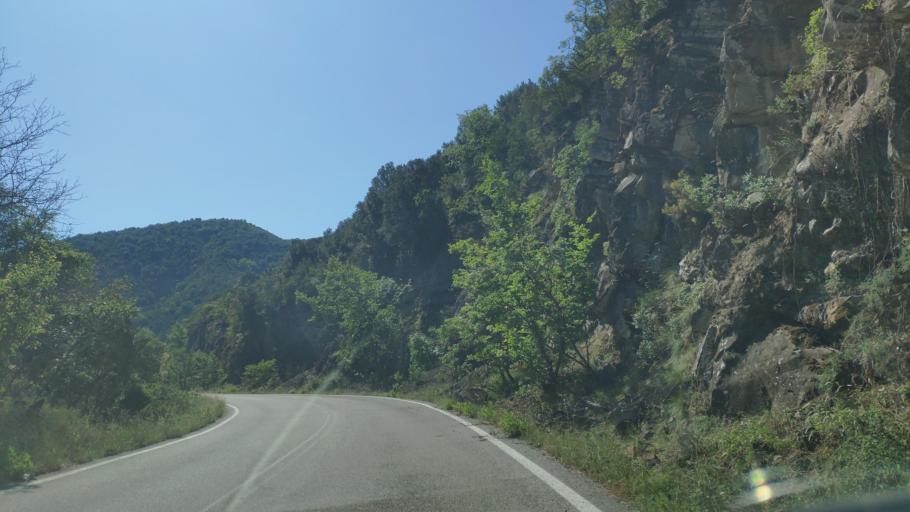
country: GR
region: West Greece
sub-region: Nomos Aitolias kai Akarnanias
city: Sardinia
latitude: 38.9226
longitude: 21.3627
